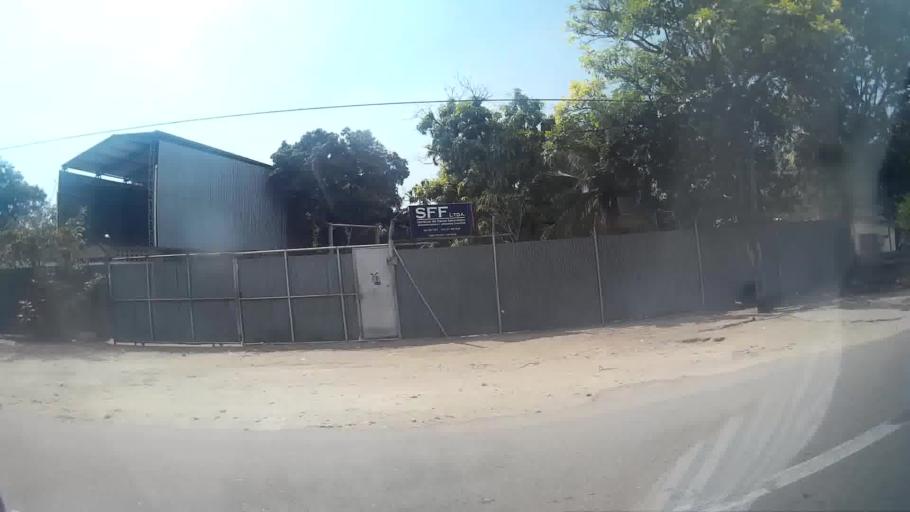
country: CO
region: Magdalena
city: Santa Marta
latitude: 11.1887
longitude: -74.2157
